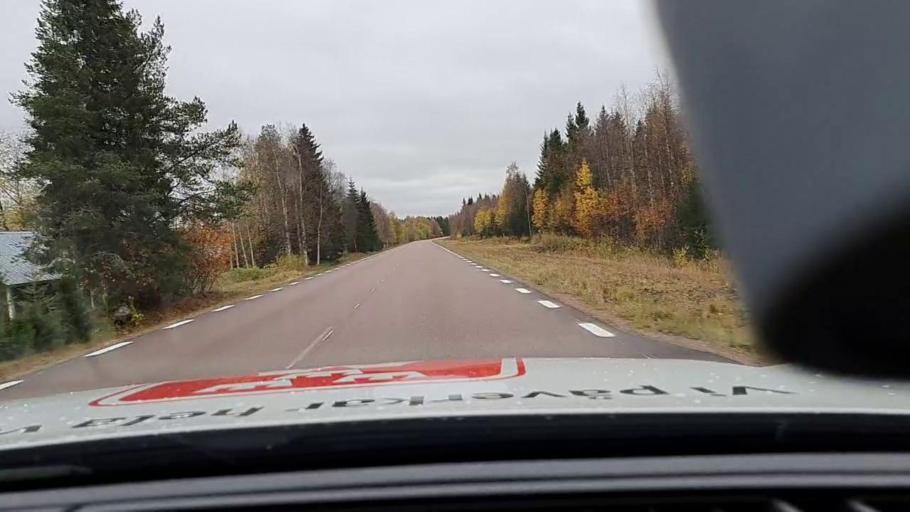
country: FI
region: Lapland
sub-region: Kemi-Tornio
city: Tornio
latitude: 66.0532
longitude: 23.9381
